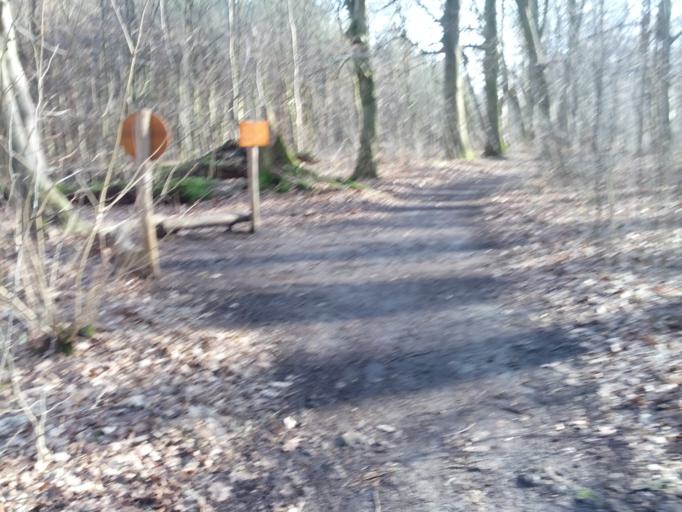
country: DE
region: Thuringia
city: Weberstedt
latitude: 51.0966
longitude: 10.5099
